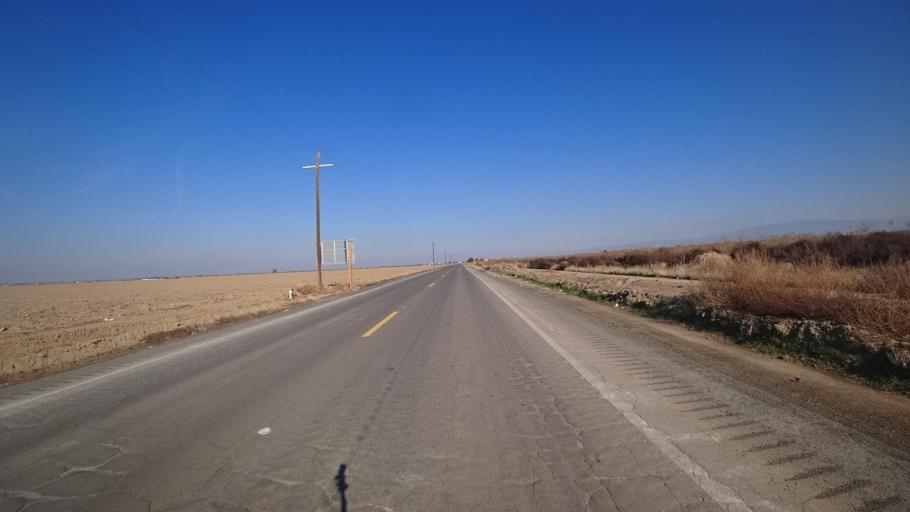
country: US
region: California
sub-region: Kern County
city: Weedpatch
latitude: 35.2114
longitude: -118.9322
